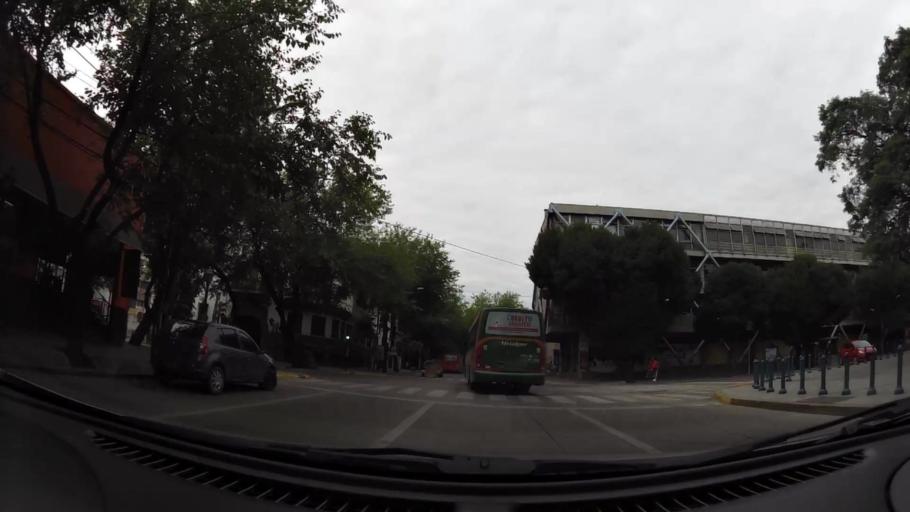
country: AR
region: Mendoza
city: Mendoza
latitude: -32.8909
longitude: -68.8436
